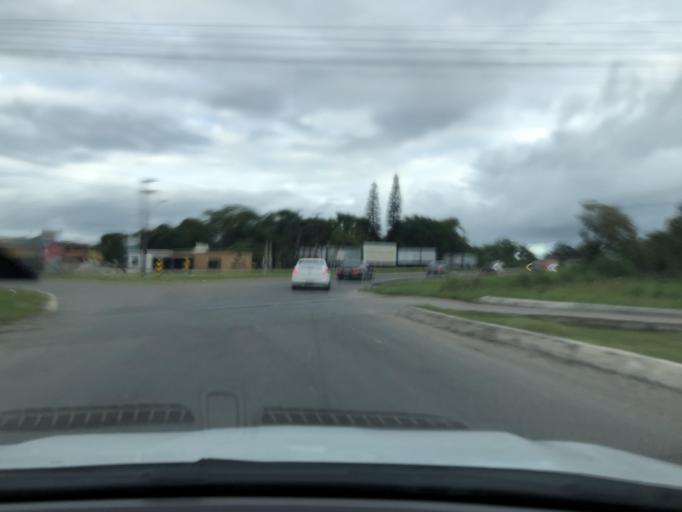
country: BR
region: Santa Catarina
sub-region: Sao Francisco Do Sul
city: Sao Francisco do Sul
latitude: -26.3718
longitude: -48.7120
